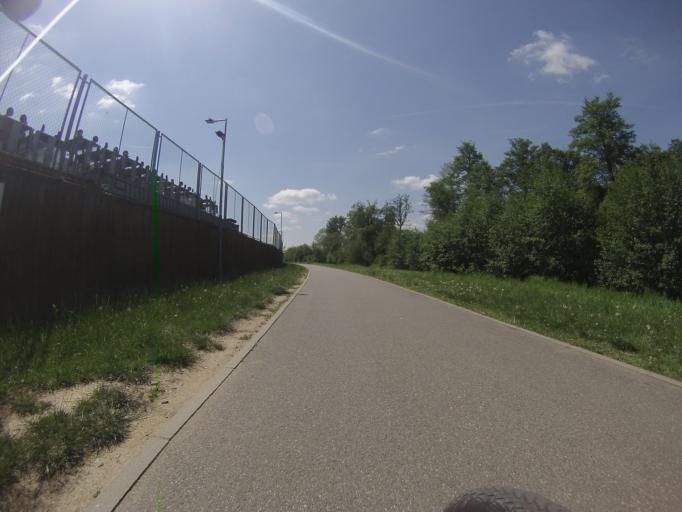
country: CZ
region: South Moravian
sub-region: Mesto Brno
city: Brno
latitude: 49.1580
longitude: 16.6258
